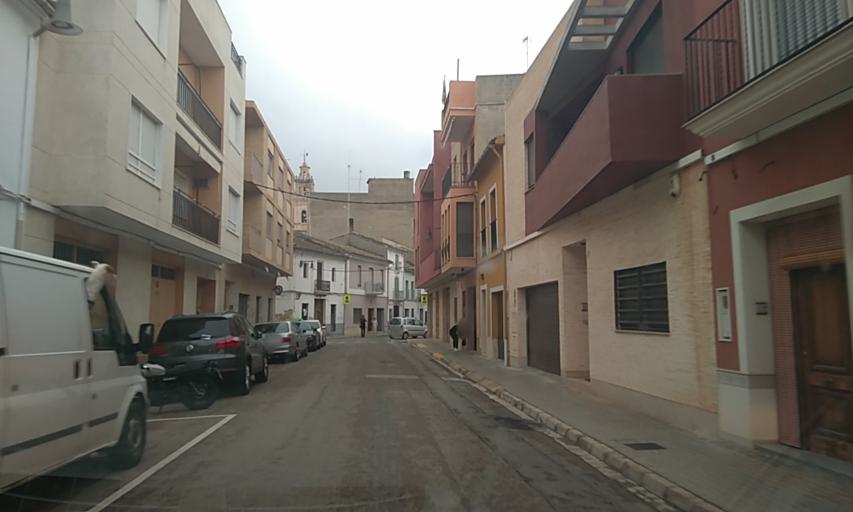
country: ES
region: Valencia
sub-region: Provincia de Valencia
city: L'Alcudia
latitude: 39.1974
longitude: -0.5082
